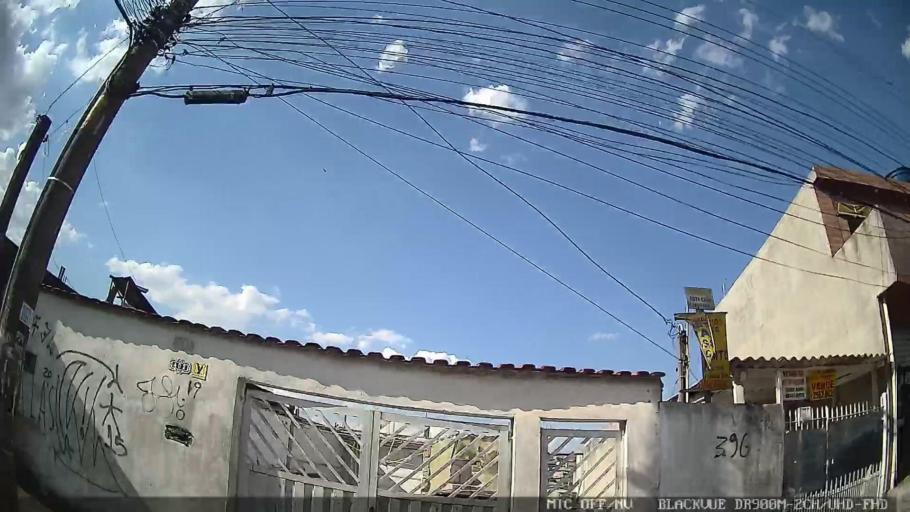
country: BR
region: Sao Paulo
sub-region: Ferraz De Vasconcelos
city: Ferraz de Vasconcelos
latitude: -23.5340
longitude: -46.4205
